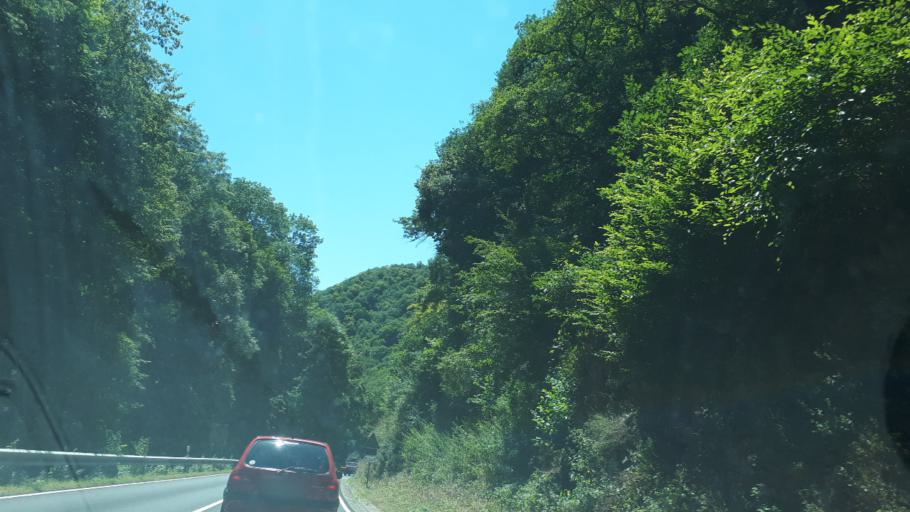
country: DE
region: Rheinland-Pfalz
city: Greimersburg
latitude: 50.1696
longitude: 7.1478
